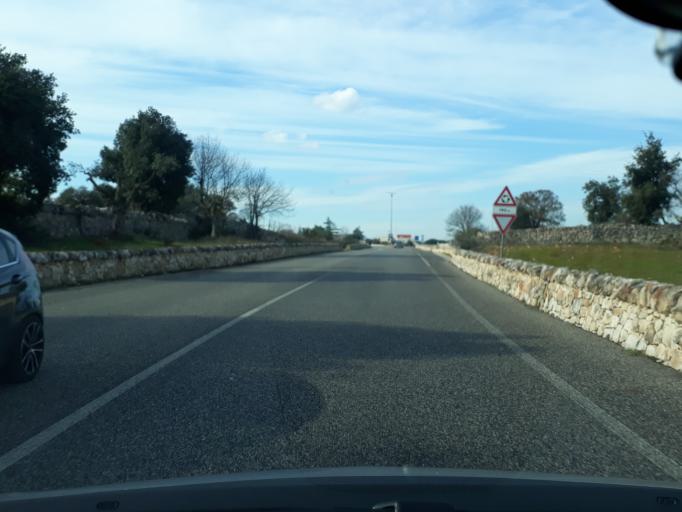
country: IT
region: Apulia
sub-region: Provincia di Bari
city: Locorotondo
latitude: 40.7608
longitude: 17.3348
